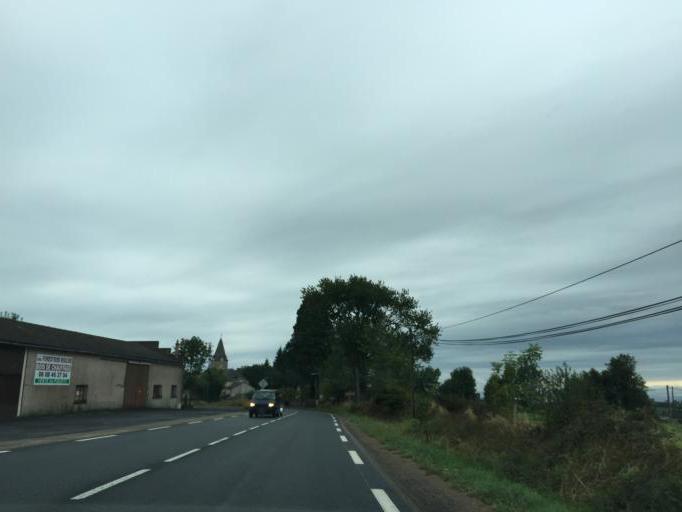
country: FR
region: Midi-Pyrenees
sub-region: Departement de l'Aveyron
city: Espalion
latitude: 44.5897
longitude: 2.7937
